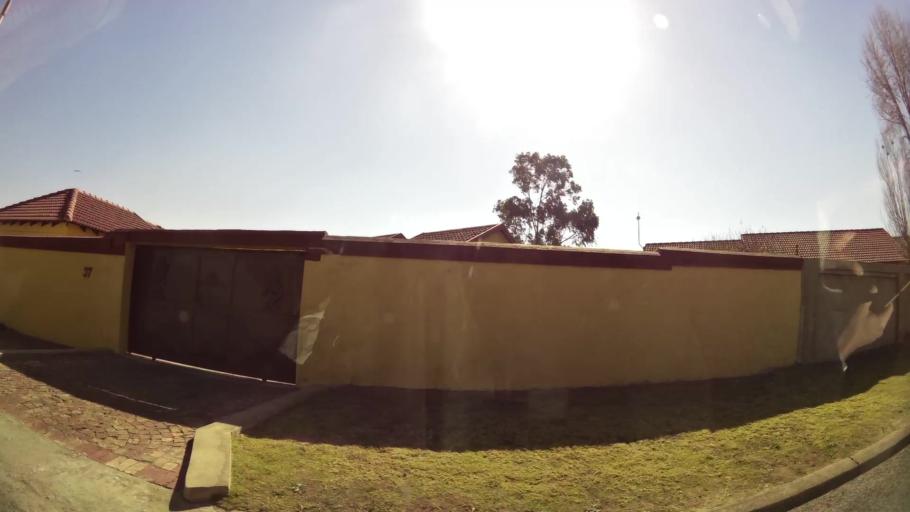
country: ZA
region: Gauteng
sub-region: Ekurhuleni Metropolitan Municipality
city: Tembisa
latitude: -26.0354
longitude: 28.2253
